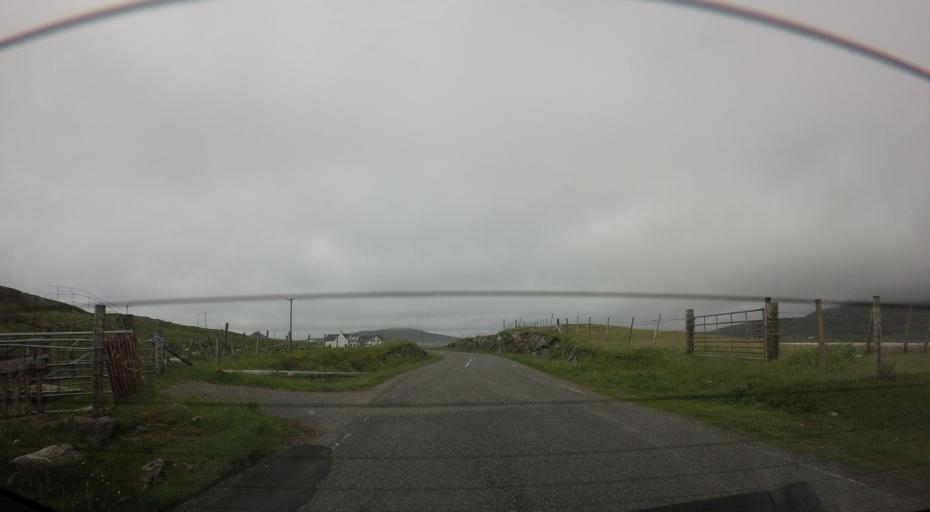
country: GB
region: Scotland
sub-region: Eilean Siar
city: Harris
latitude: 57.8656
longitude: -6.9538
